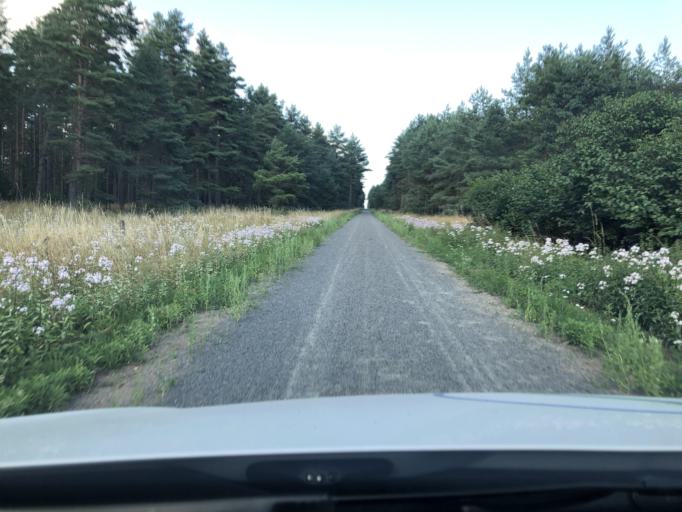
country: SE
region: Skane
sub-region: Kristianstads Kommun
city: Norra Asum
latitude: 55.9231
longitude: 14.1253
